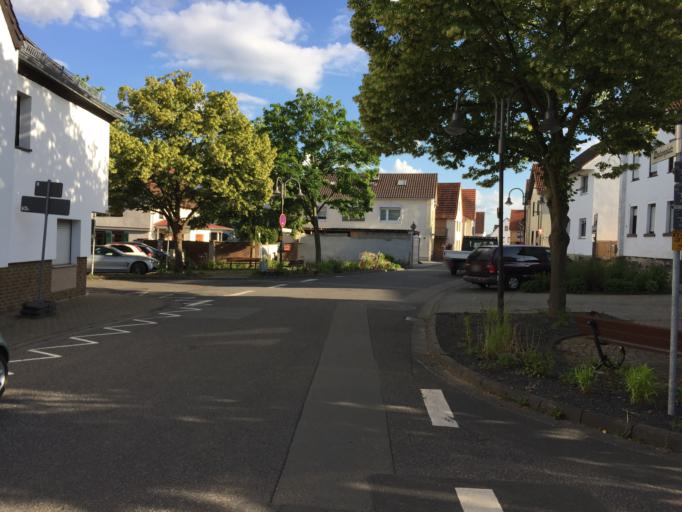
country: DE
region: Hesse
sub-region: Regierungsbezirk Darmstadt
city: Niederdorfelden
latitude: 50.2139
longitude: 8.7914
